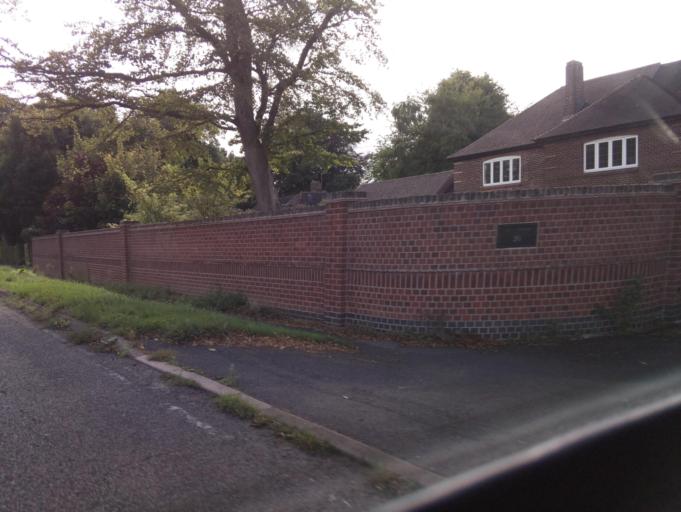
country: GB
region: England
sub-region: Leicestershire
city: Ashby de la Zouch
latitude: 52.7348
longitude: -1.4836
